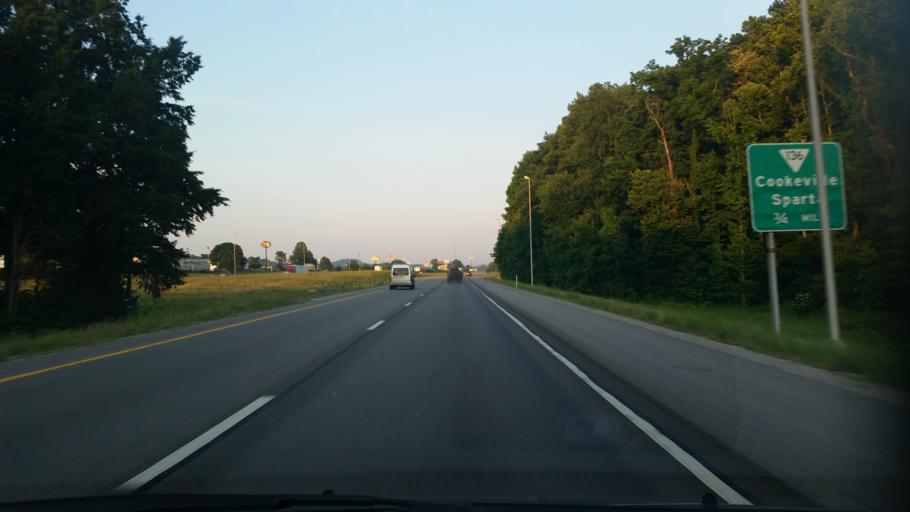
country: US
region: Tennessee
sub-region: Putnam County
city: Cookeville
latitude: 36.1362
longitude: -85.5189
